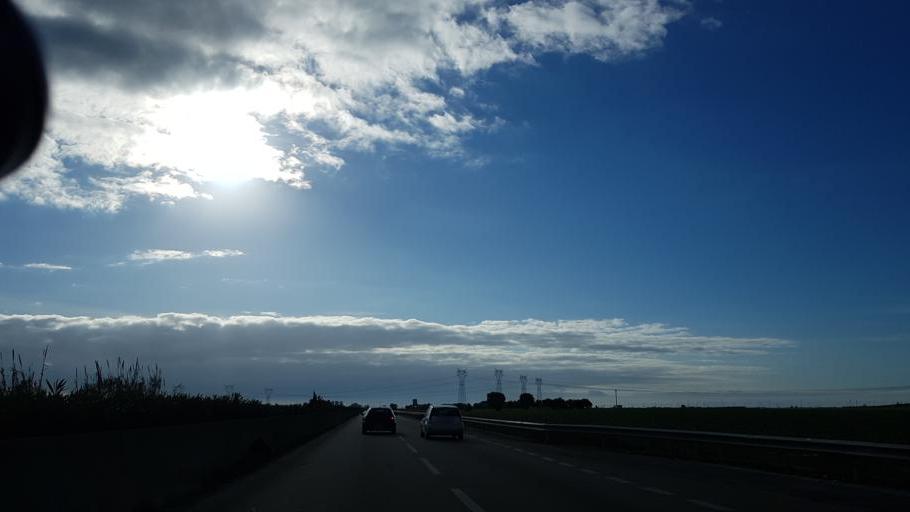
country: IT
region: Apulia
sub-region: Provincia di Brindisi
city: Tuturano
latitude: 40.5670
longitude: 17.9860
